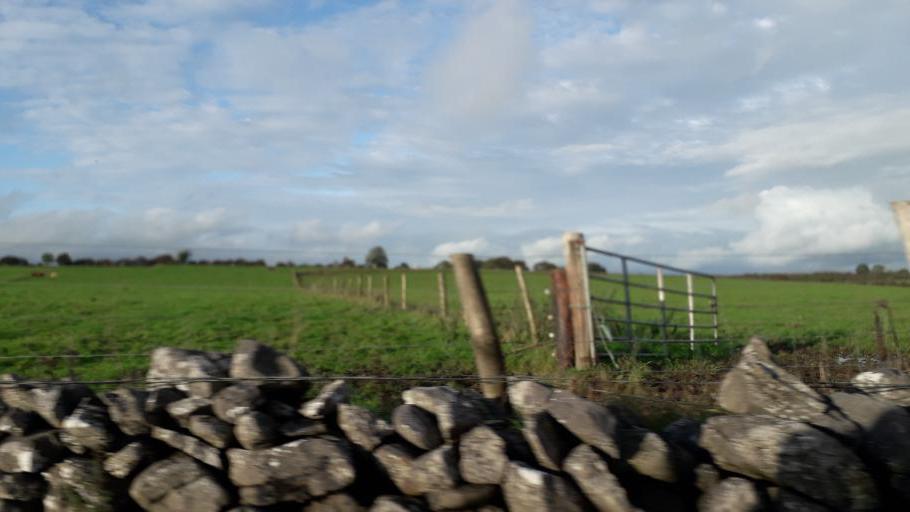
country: IE
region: Connaught
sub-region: Roscommon
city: Roscommon
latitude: 53.7690
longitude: -8.2188
